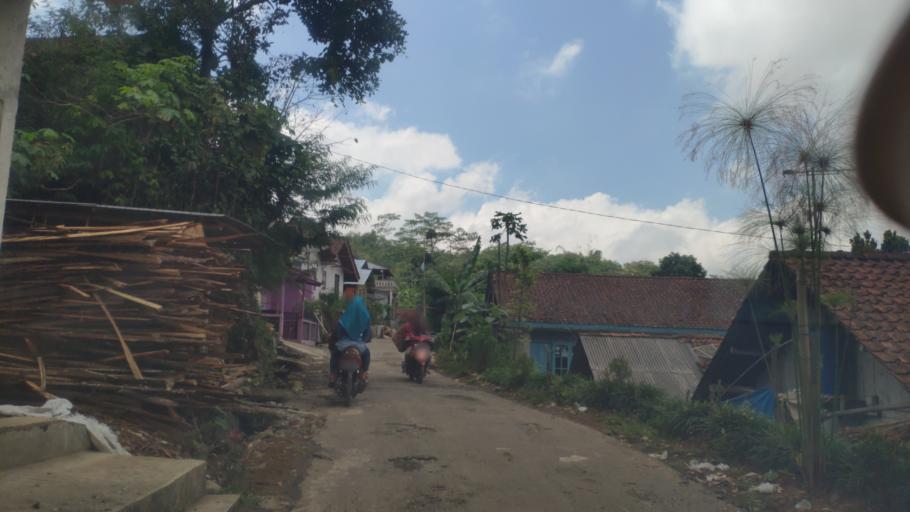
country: ID
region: Central Java
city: Wonosobo
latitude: -7.2822
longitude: 109.7501
